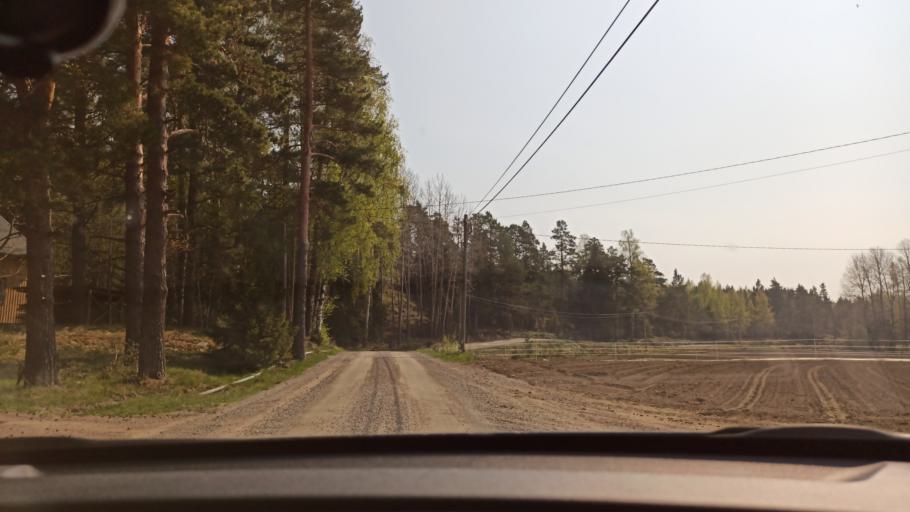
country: FI
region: Uusimaa
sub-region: Helsinki
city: Espoo
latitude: 60.1097
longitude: 24.6313
